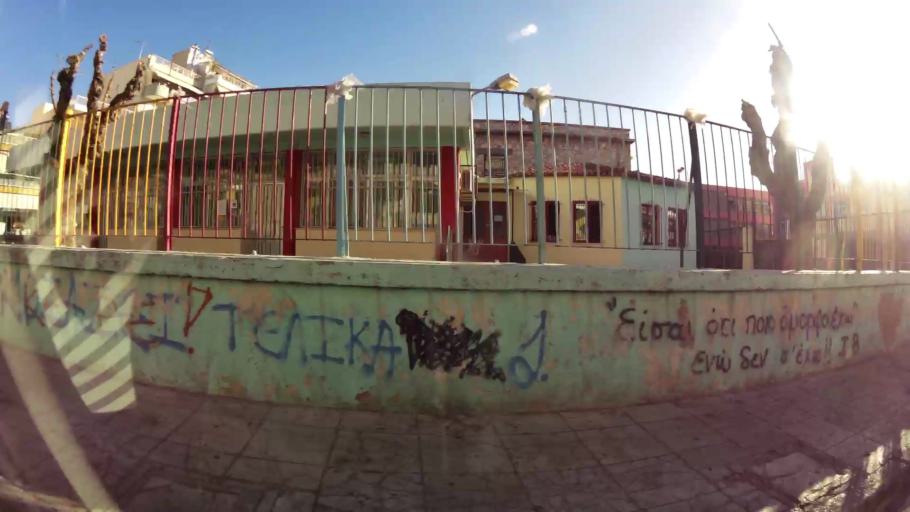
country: GR
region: Attica
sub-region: Nomos Piraios
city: Nikaia
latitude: 37.9728
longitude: 23.6573
